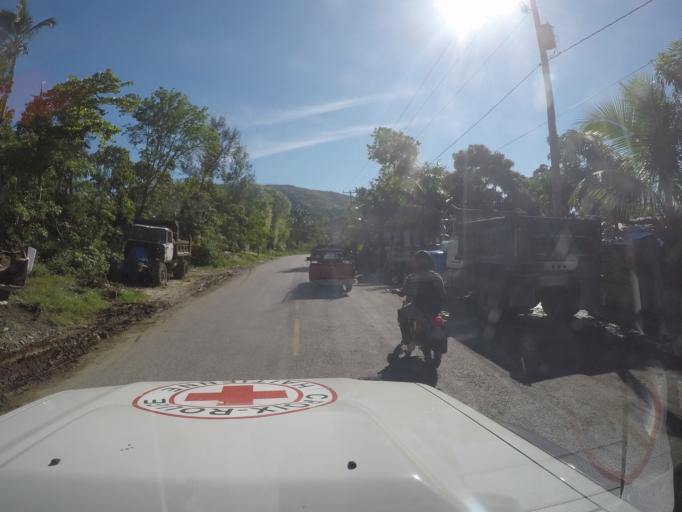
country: HT
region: Ouest
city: Leogane
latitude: 18.4516
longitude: -72.6538
